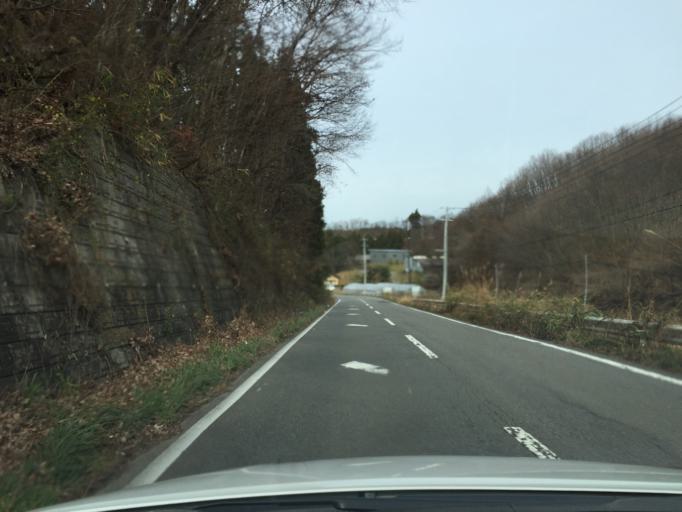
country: JP
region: Fukushima
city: Ishikawa
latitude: 37.2306
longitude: 140.6300
